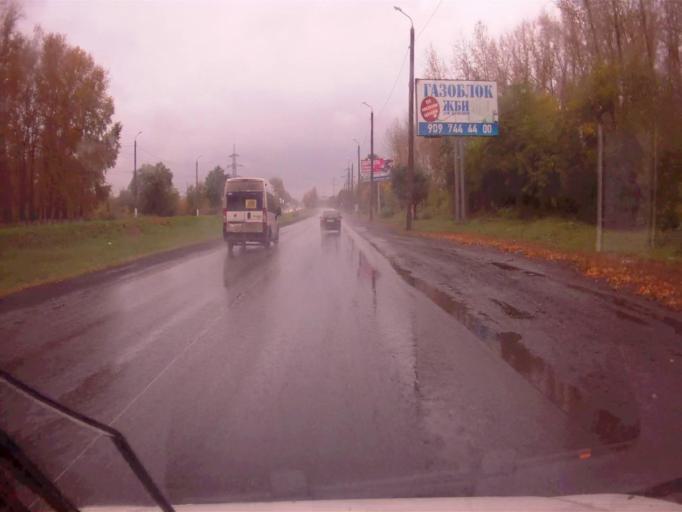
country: RU
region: Chelyabinsk
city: Dolgoderevenskoye
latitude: 55.2447
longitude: 61.3597
